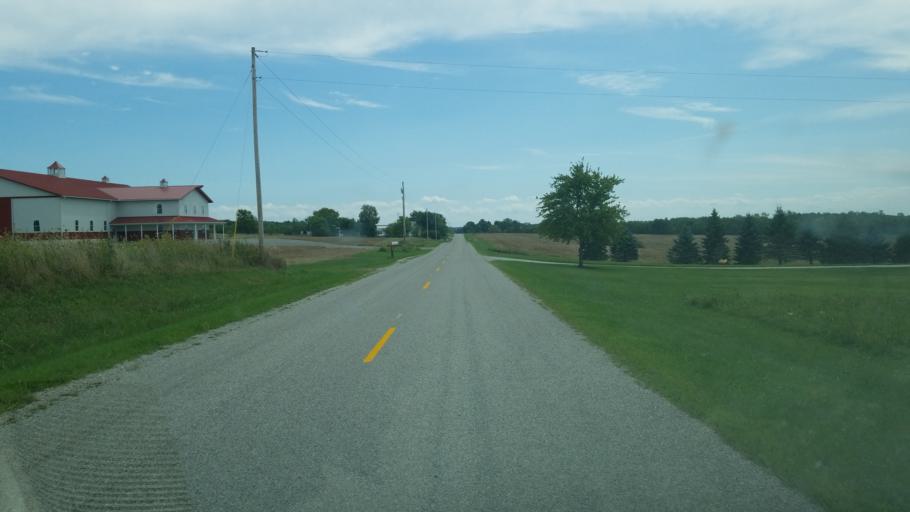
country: US
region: Ohio
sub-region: Hardin County
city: Kenton
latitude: 40.6149
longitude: -83.4095
